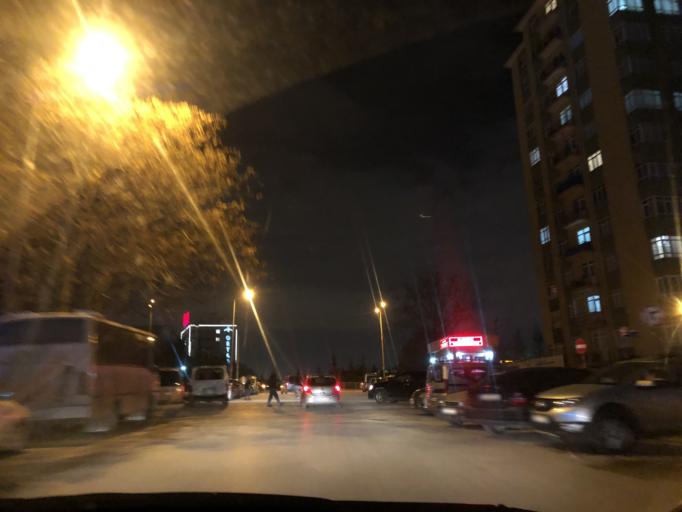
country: TR
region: Ankara
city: Batikent
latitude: 39.9645
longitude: 32.7967
